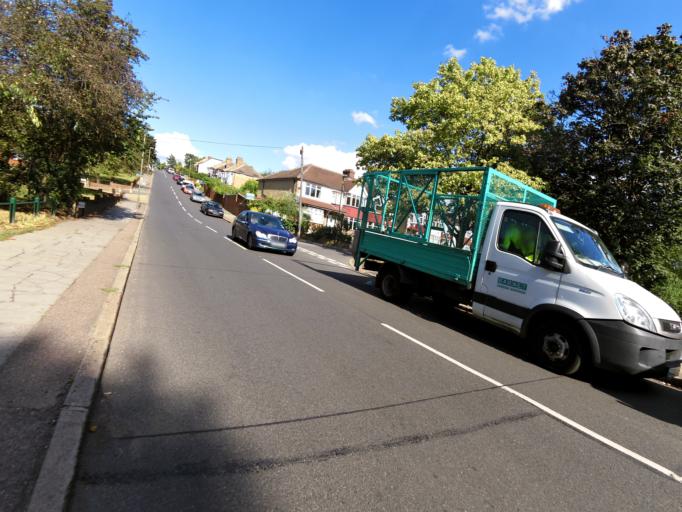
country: GB
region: England
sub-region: Greater London
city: Hadley Wood
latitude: 51.6355
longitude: -0.1497
